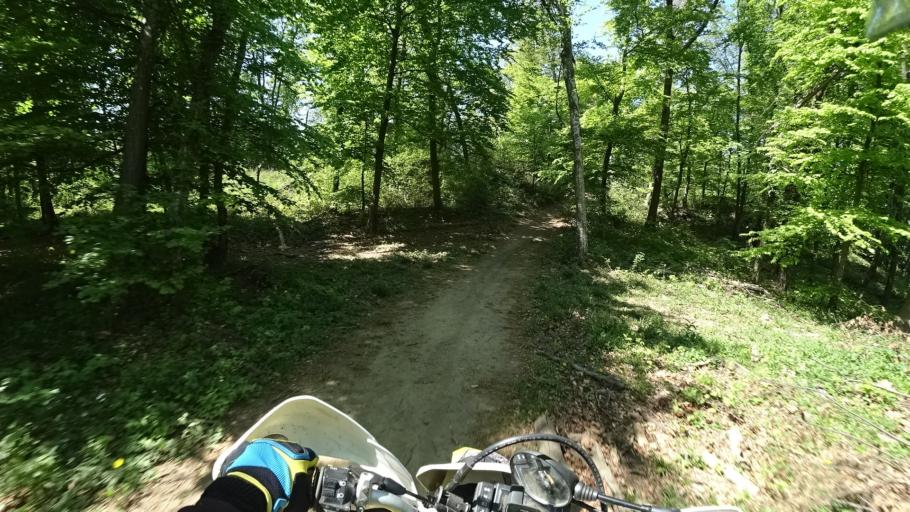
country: HR
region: Zagrebacka
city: Jablanovec
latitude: 45.8676
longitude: 15.8562
